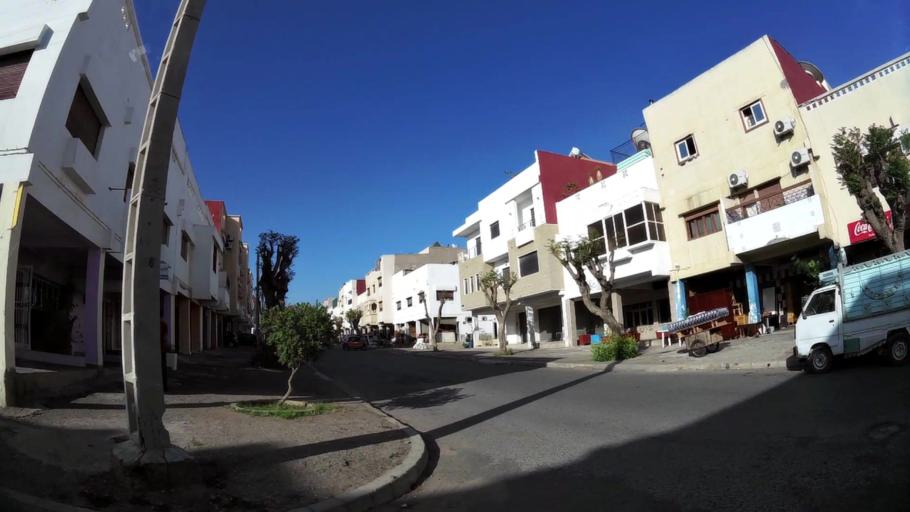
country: MA
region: Souss-Massa-Draa
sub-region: Agadir-Ida-ou-Tnan
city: Agadir
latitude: 30.4292
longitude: -9.5799
